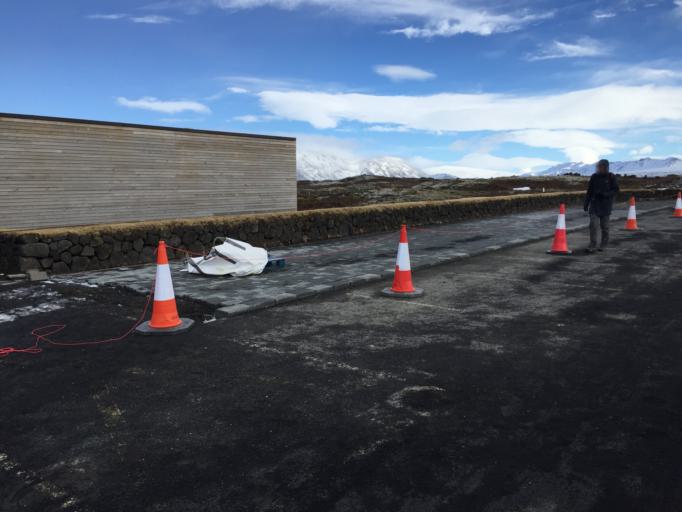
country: IS
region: South
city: Hveragerdi
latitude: 64.2557
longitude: -21.1311
